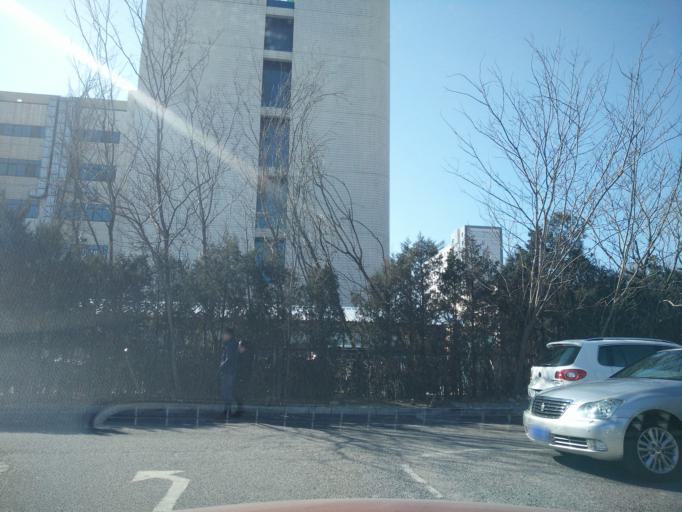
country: CN
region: Beijing
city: Jiugong
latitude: 39.7967
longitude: 116.5057
